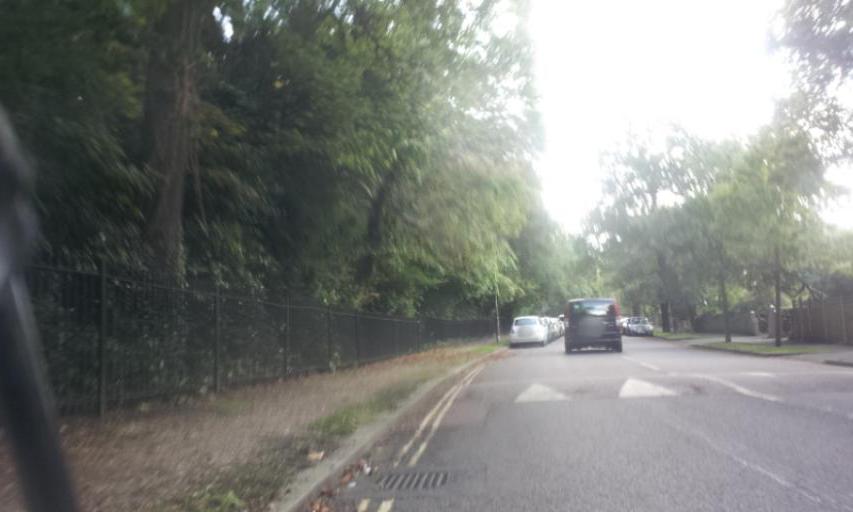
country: GB
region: England
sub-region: Greater London
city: Thornton Heath
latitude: 51.4317
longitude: -0.0779
